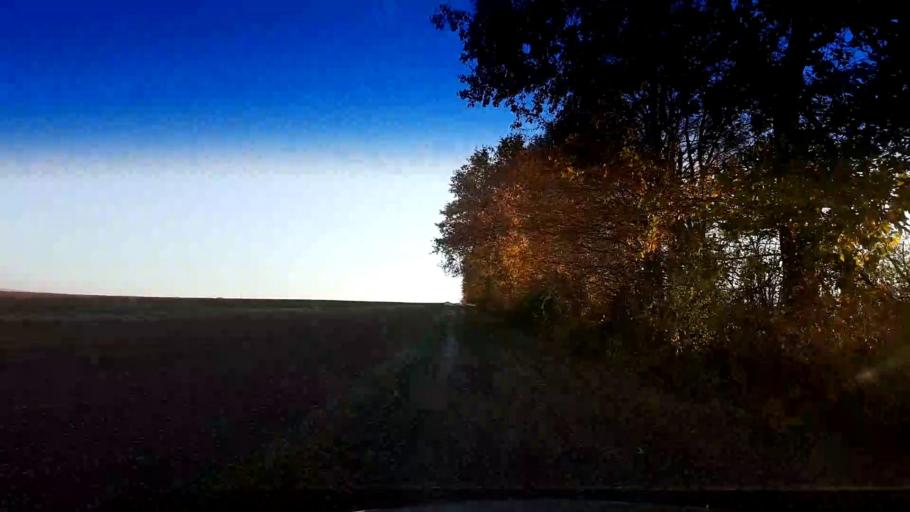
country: DE
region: Bavaria
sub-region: Upper Franconia
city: Memmelsdorf
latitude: 49.9727
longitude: 10.9721
